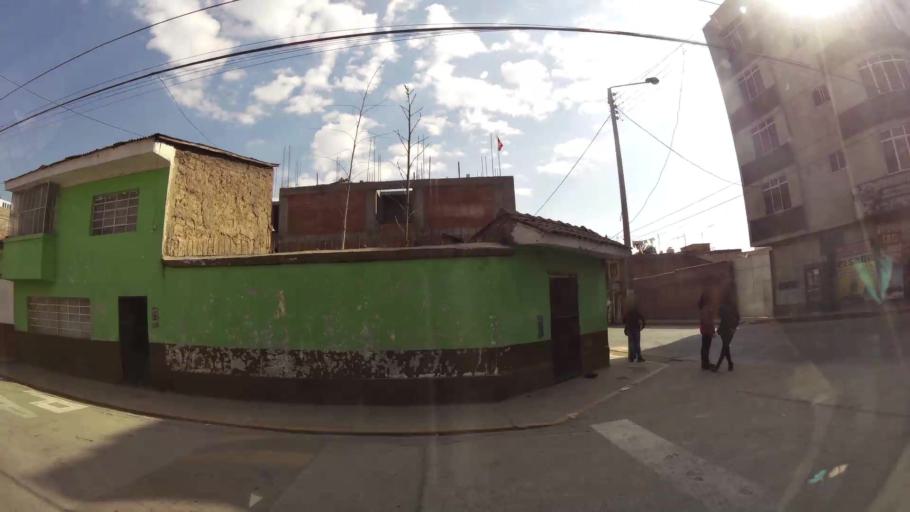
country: PE
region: Junin
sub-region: Provincia de Huancayo
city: El Tambo
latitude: -12.0607
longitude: -75.2127
